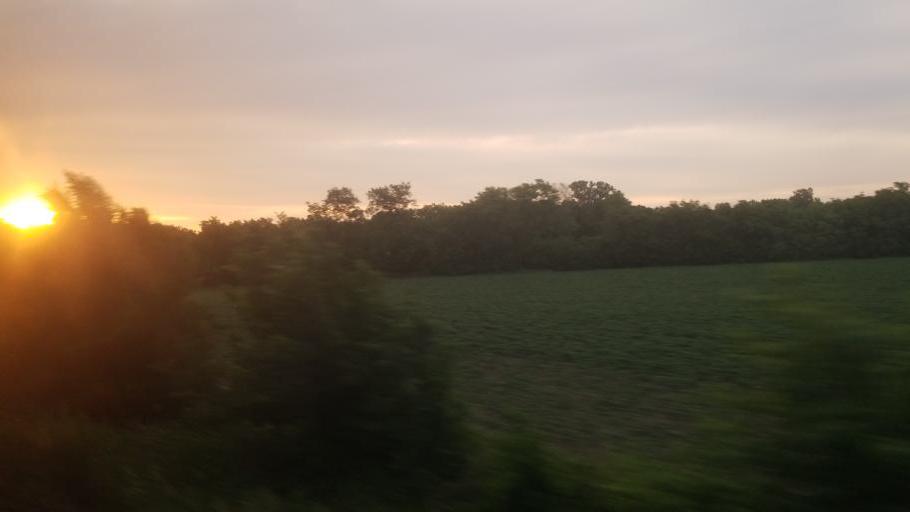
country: US
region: Kansas
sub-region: Marion County
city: Peabody
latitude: 38.1567
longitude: -97.1175
